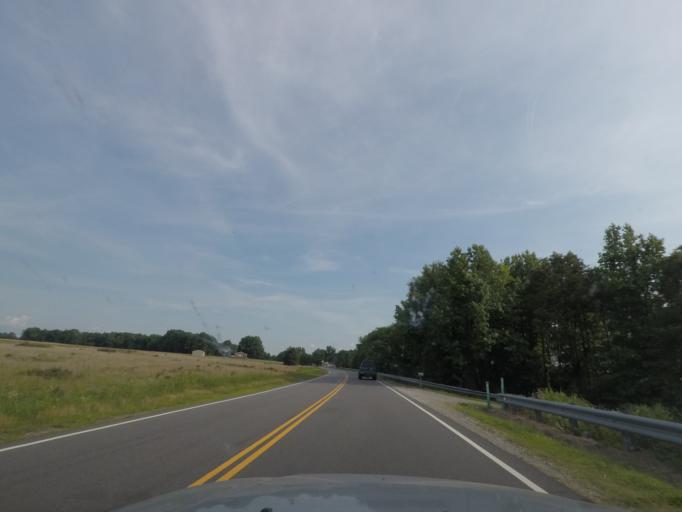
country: US
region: Virginia
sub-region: Mecklenburg County
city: Clarksville
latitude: 36.7417
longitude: -78.6375
